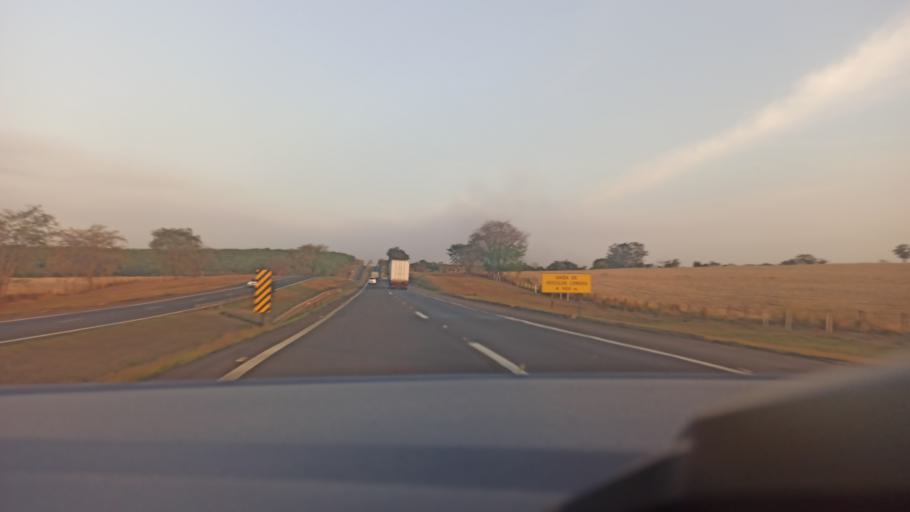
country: BR
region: Sao Paulo
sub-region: Taquaritinga
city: Taquaritinga
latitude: -21.4465
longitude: -48.6408
